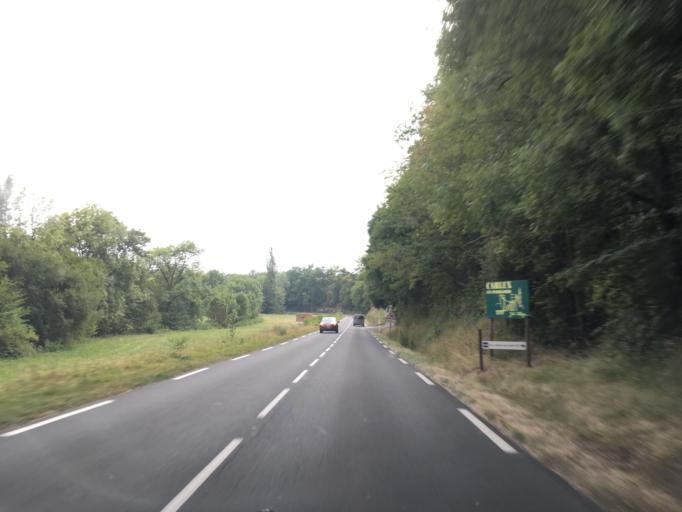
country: FR
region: Aquitaine
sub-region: Departement de la Dordogne
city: Eyvigues-et-Eybenes
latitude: 44.8852
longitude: 1.3805
